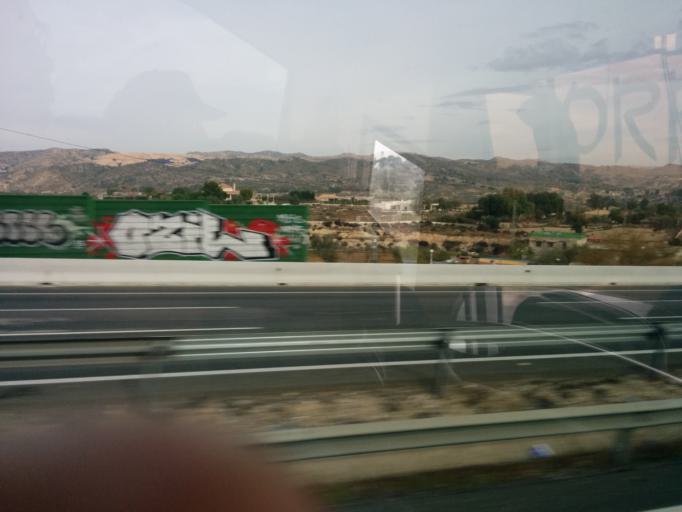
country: ES
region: Valencia
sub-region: Provincia de Alicante
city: Elche
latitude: 38.2891
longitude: -0.7114
